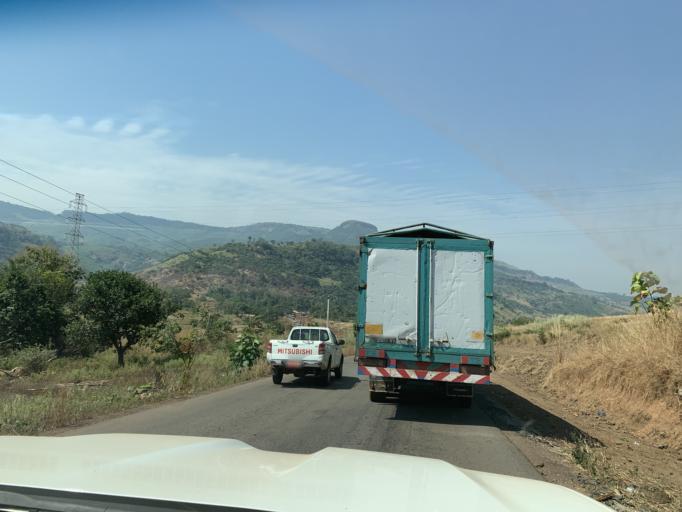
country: GN
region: Mamou
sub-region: Mamou Prefecture
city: Mamou
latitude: 10.1940
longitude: -12.4600
